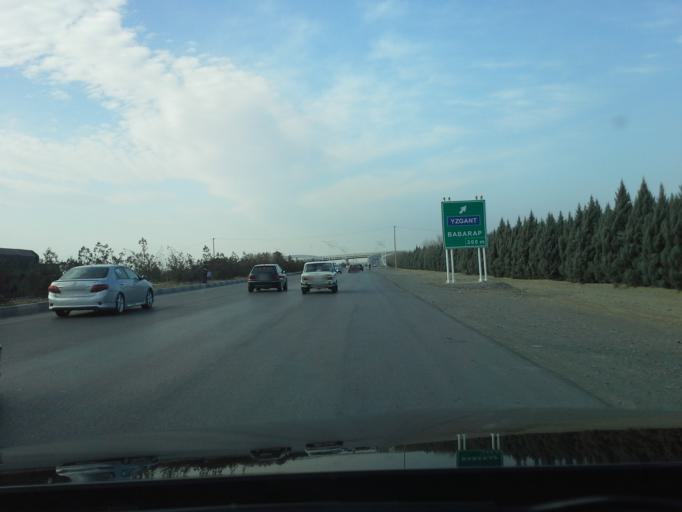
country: TM
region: Ahal
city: Abadan
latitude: 38.0858
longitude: 58.1173
